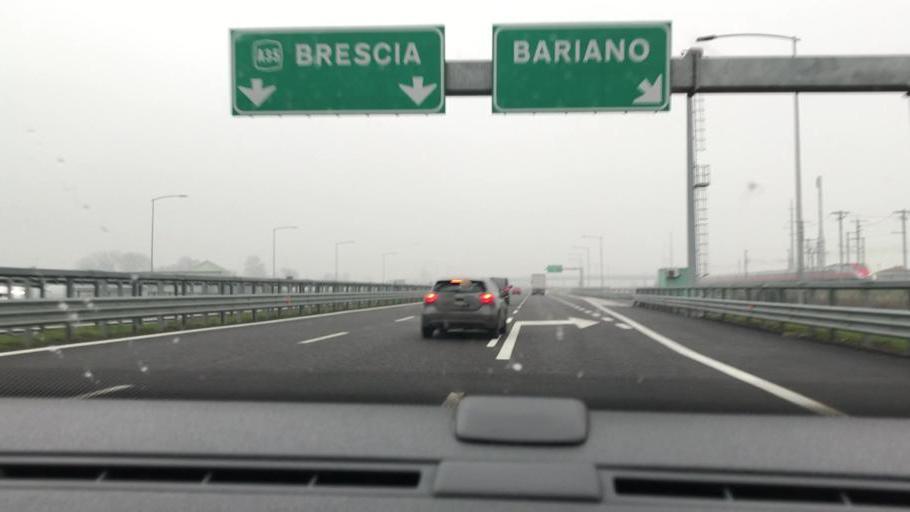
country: IT
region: Lombardy
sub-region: Provincia di Bergamo
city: Fornovo San Giovanni
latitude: 45.5092
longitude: 9.6866
